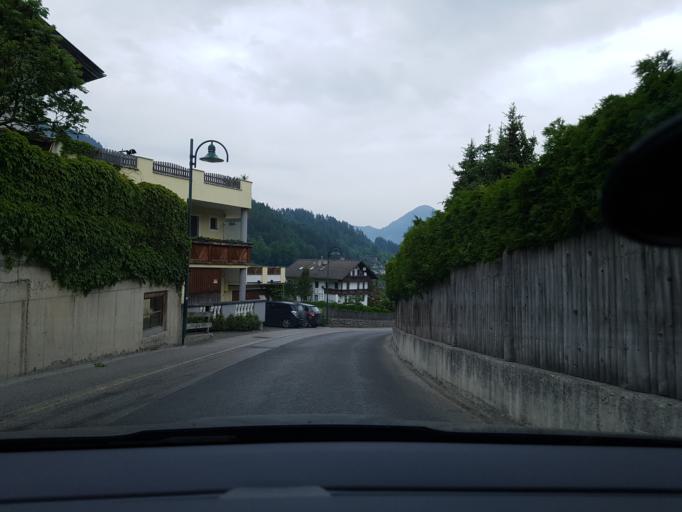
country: AT
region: Tyrol
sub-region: Politischer Bezirk Schwaz
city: Fugen
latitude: 47.3426
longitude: 11.8468
